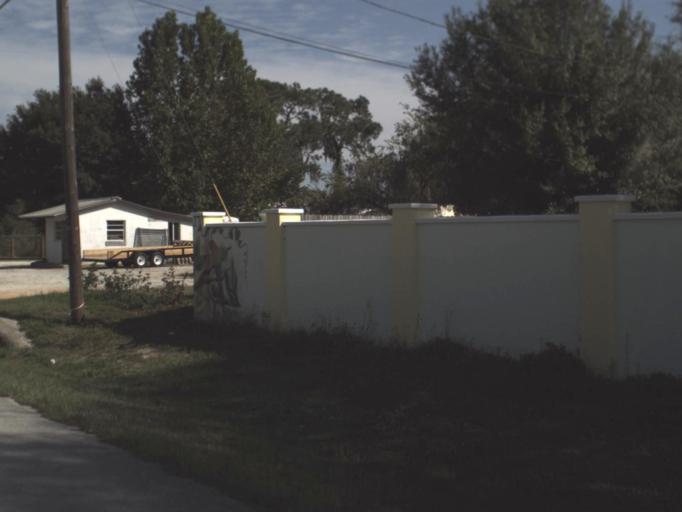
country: US
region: Florida
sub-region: Highlands County
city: Sebring
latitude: 27.5449
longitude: -81.4533
